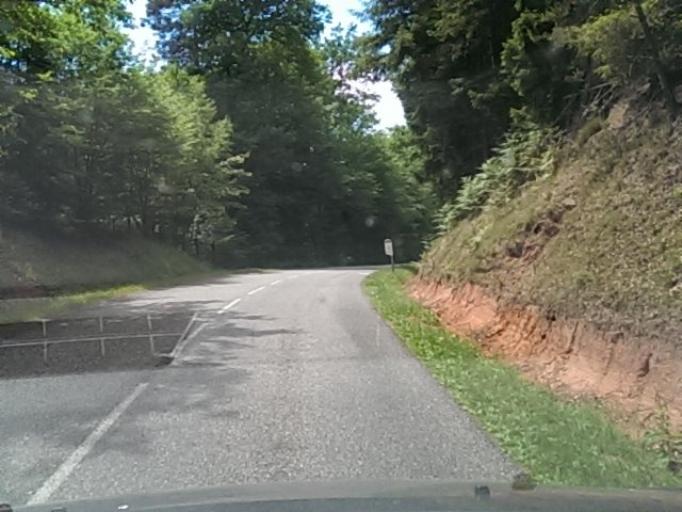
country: FR
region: Lorraine
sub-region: Departement de la Moselle
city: Lemberg
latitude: 48.9912
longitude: 7.4113
